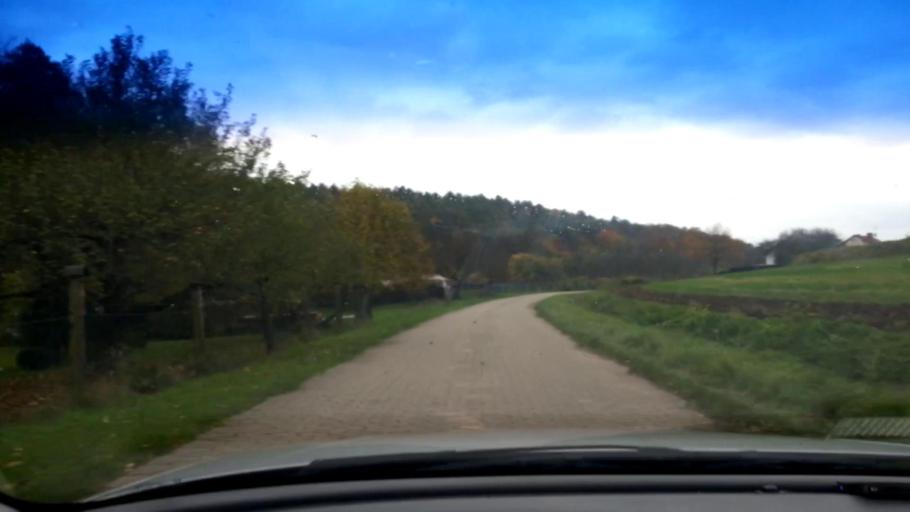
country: DE
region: Bavaria
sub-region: Regierungsbezirk Unterfranken
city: Stettfeld
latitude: 49.9772
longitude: 10.7310
